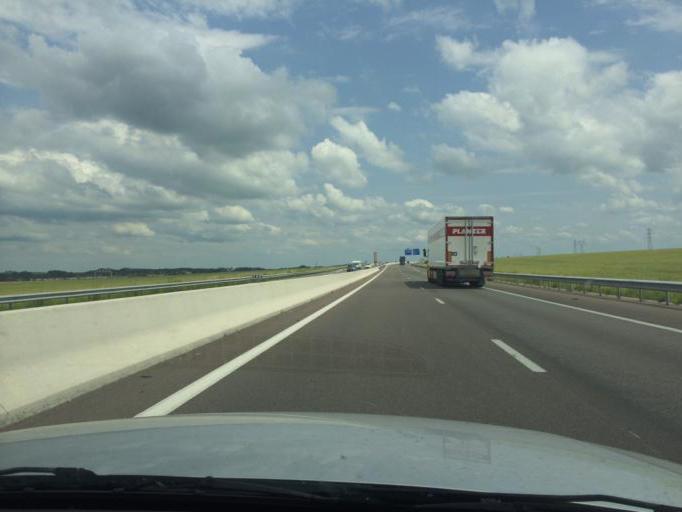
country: FR
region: Champagne-Ardenne
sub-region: Departement de la Marne
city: Taissy
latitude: 49.2077
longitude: 4.0762
